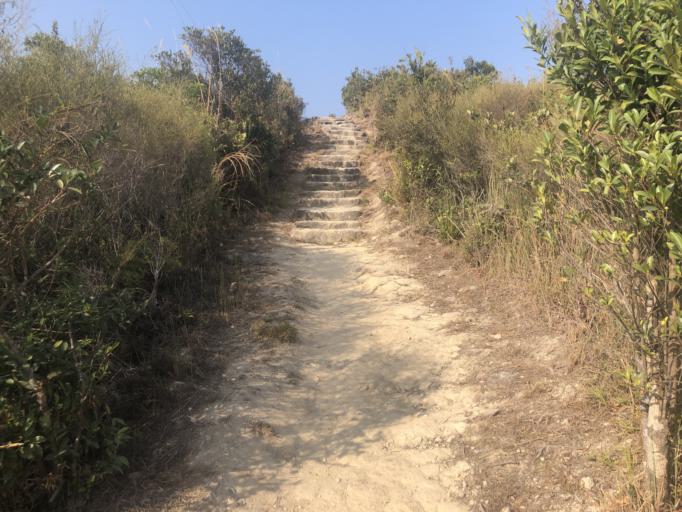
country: HK
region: Sai Kung
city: Sai Kung
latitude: 22.3584
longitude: 114.2954
